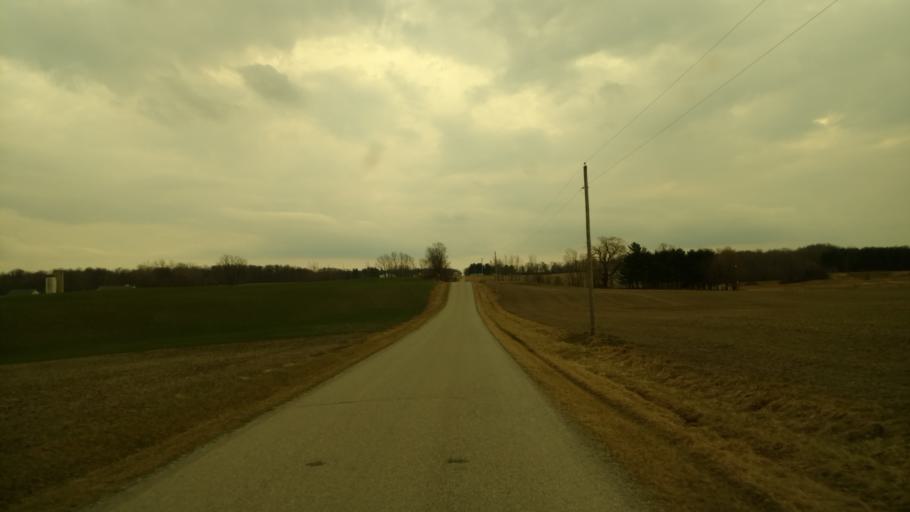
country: US
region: Ohio
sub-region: Richland County
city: Lexington
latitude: 40.6401
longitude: -82.6900
